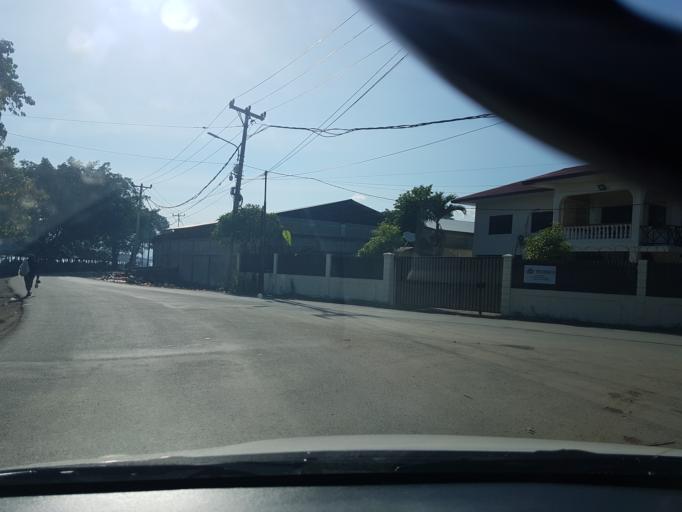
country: TL
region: Dili
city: Dili
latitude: -8.5412
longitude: 125.5426
